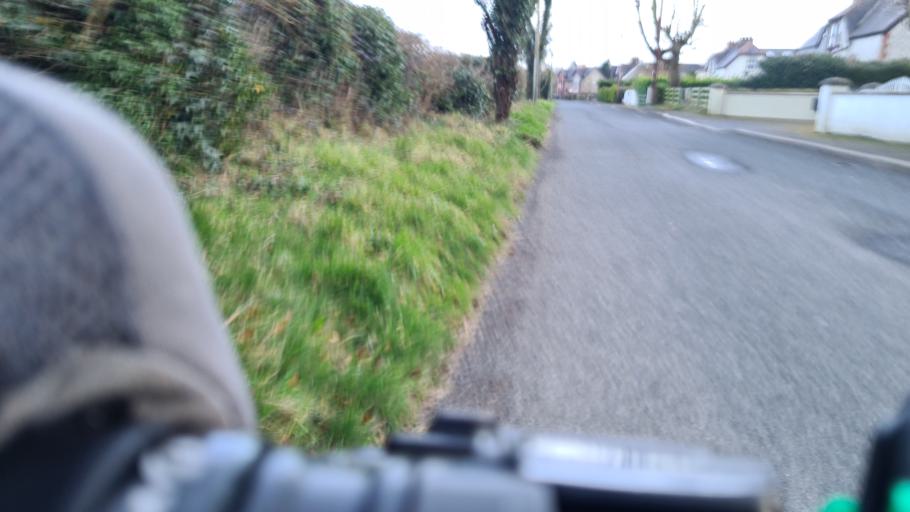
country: IE
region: Leinster
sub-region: Kildare
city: Celbridge
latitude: 53.3348
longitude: -6.5719
